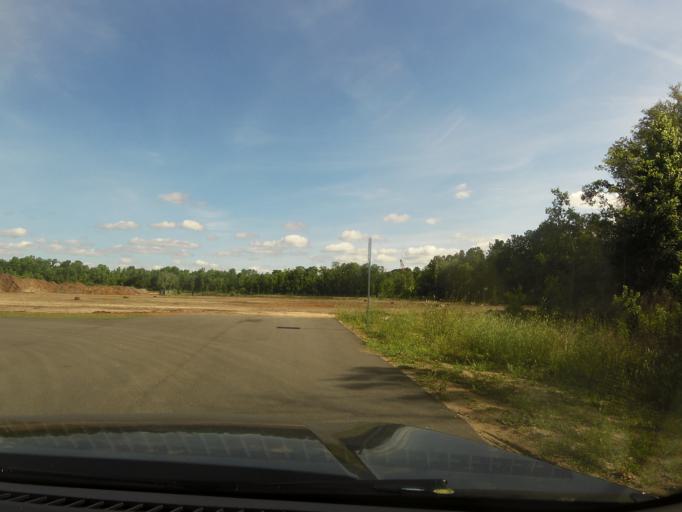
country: US
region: Florida
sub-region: Nassau County
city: Callahan
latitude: 30.5693
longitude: -81.8372
